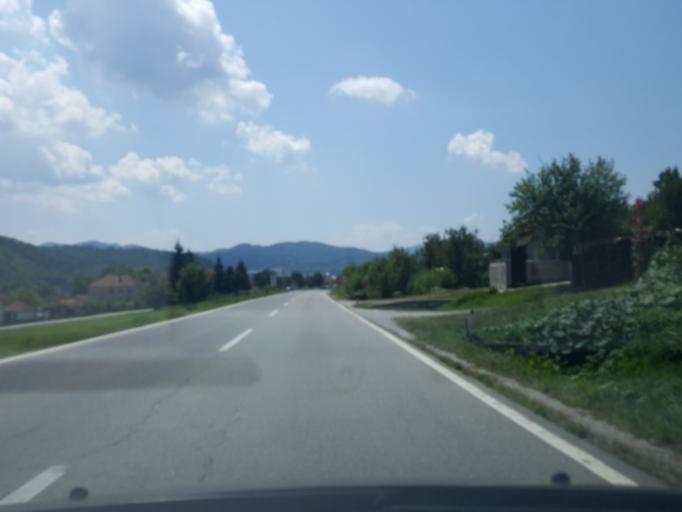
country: RS
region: Central Serbia
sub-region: Moravicki Okrug
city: Gornji Milanovac
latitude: 44.0649
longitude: 20.4913
